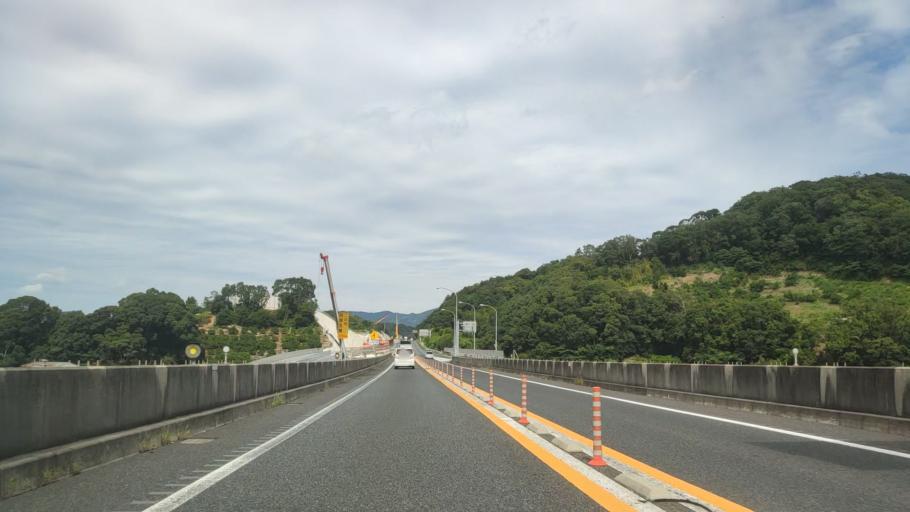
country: JP
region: Wakayama
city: Kainan
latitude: 34.0284
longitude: 135.2009
